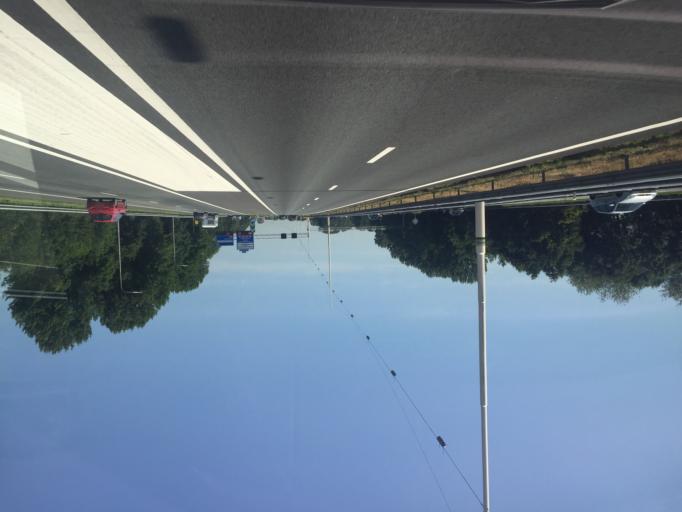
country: NL
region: Utrecht
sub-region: Gemeente Utrecht
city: Lunetten
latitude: 52.0587
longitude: 5.1571
